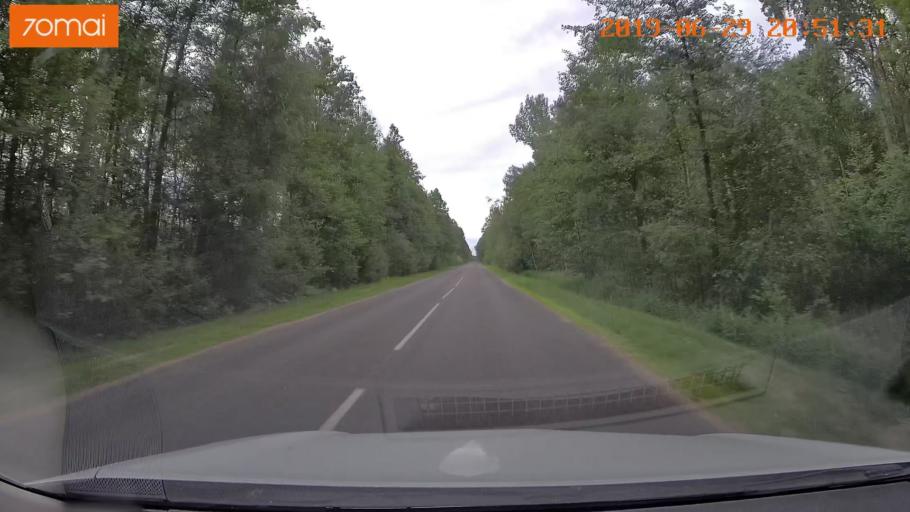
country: BY
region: Brest
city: Hantsavichy
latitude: 52.6889
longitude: 26.3505
